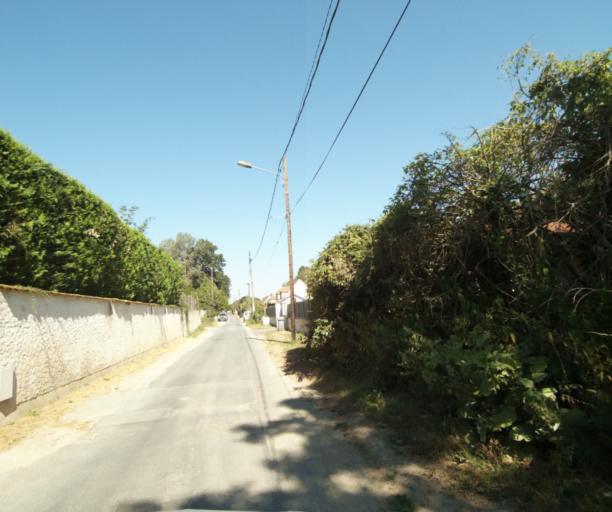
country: FR
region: Ile-de-France
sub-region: Departement de l'Essonne
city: Itteville
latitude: 48.5314
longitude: 2.3578
